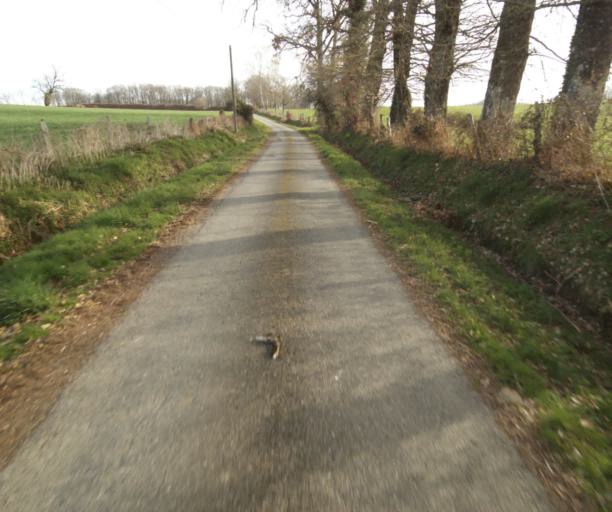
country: FR
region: Limousin
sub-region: Departement de la Correze
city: Chamboulive
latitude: 45.4355
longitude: 1.7382
